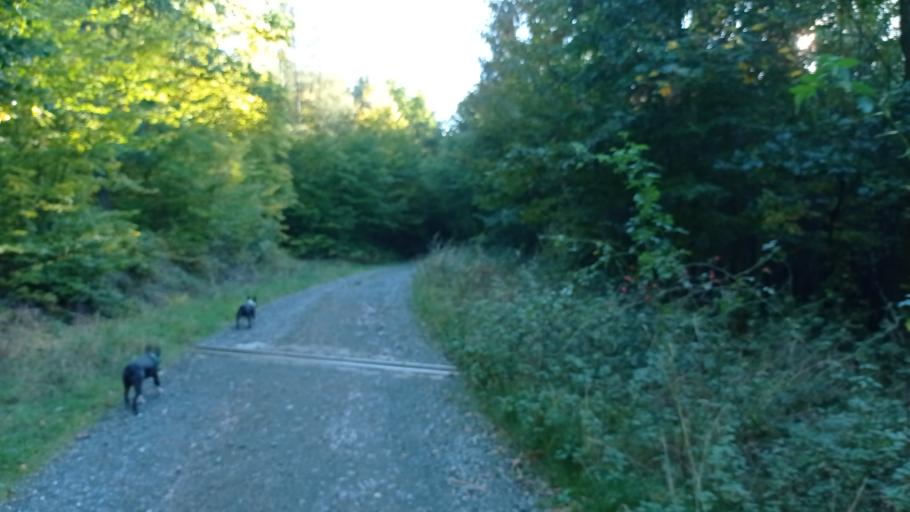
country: CZ
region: Central Bohemia
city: Chynava
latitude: 50.0623
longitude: 14.0592
